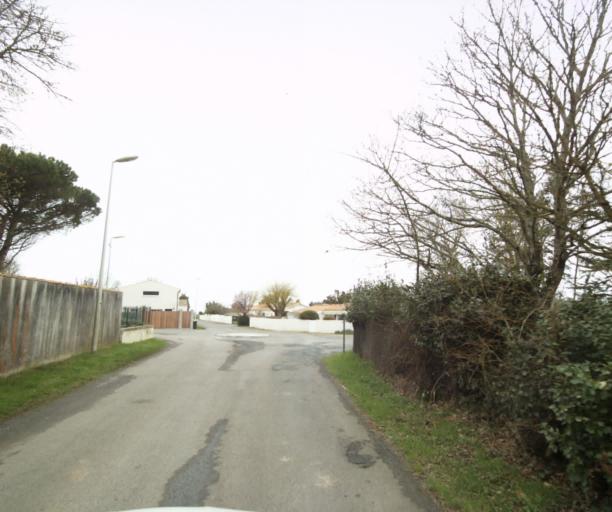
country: FR
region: Poitou-Charentes
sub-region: Departement de la Charente-Maritime
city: Nieul-sur-Mer
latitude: 46.1937
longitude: -1.1717
